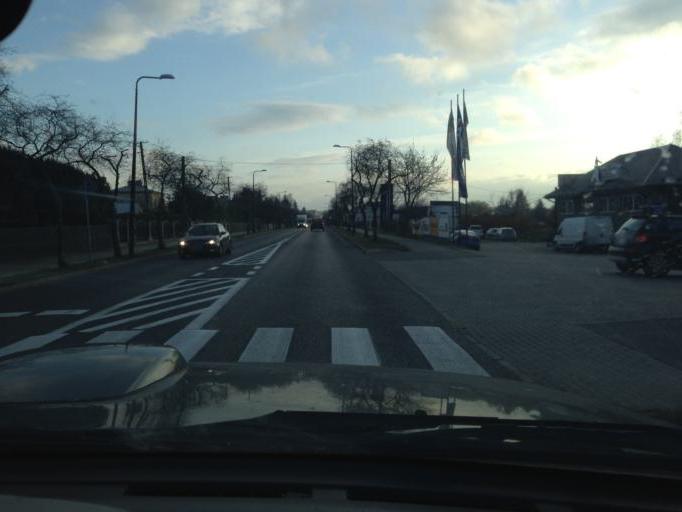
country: PL
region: Subcarpathian Voivodeship
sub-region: Powiat jasielski
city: Jaslo
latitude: 49.7599
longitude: 21.4709
